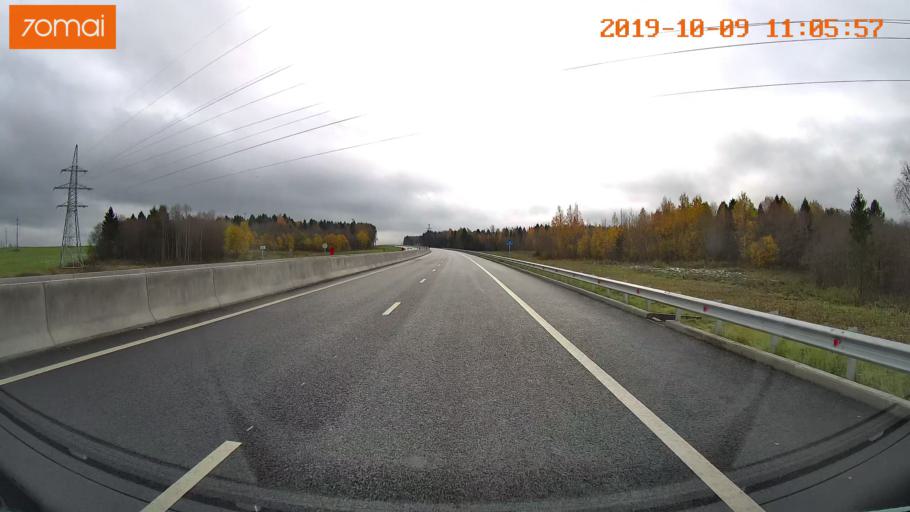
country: RU
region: Vologda
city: Molochnoye
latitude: 59.1929
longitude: 39.7582
